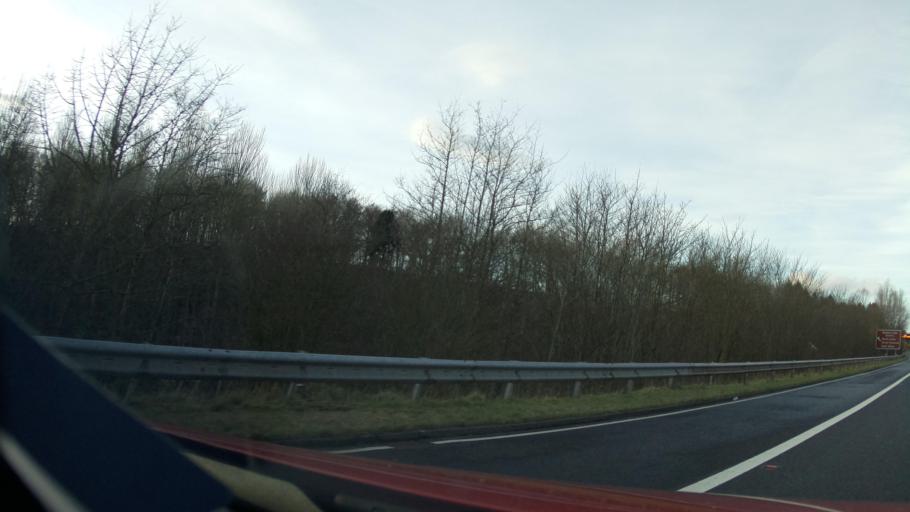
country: GB
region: England
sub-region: Cumbria
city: Penrith
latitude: 54.6408
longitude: -2.7339
